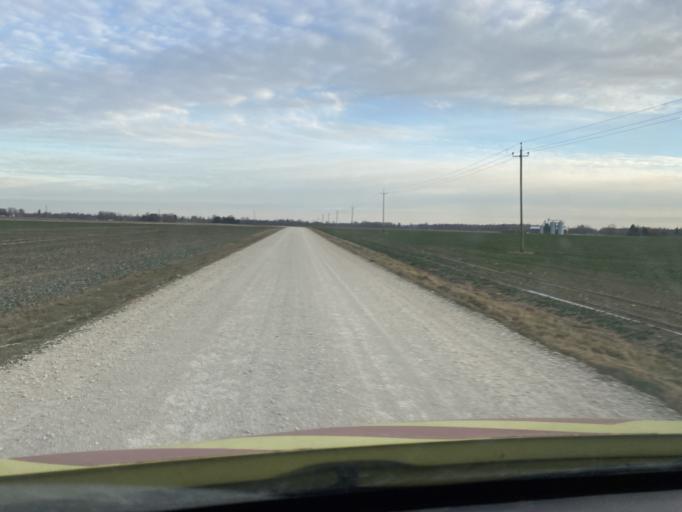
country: EE
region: Jogevamaa
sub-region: Poltsamaa linn
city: Poltsamaa
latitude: 58.5814
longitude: 26.0760
